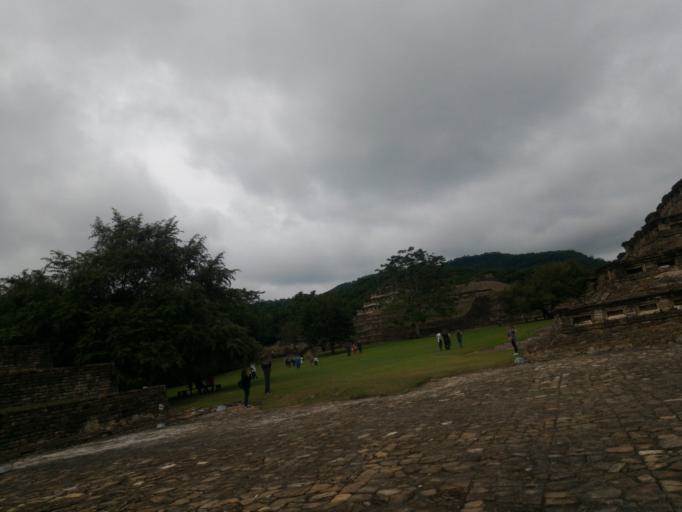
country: MX
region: Veracruz
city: Papantla de Olarte
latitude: 20.4460
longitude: -97.3779
